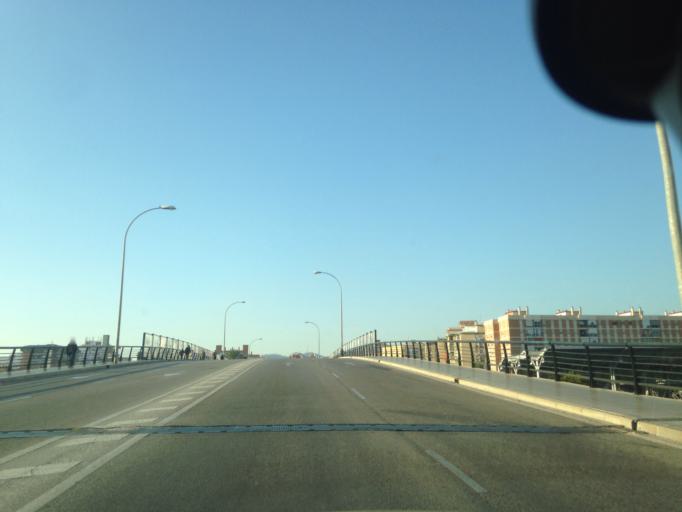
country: ES
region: Andalusia
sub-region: Provincia de Malaga
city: Malaga
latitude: 36.7087
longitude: -4.4362
